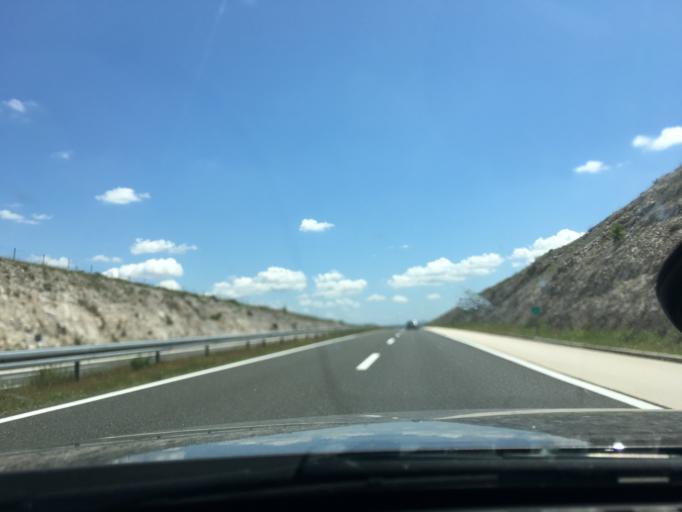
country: HR
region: Zadarska
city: Polaca
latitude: 44.0757
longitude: 15.5138
